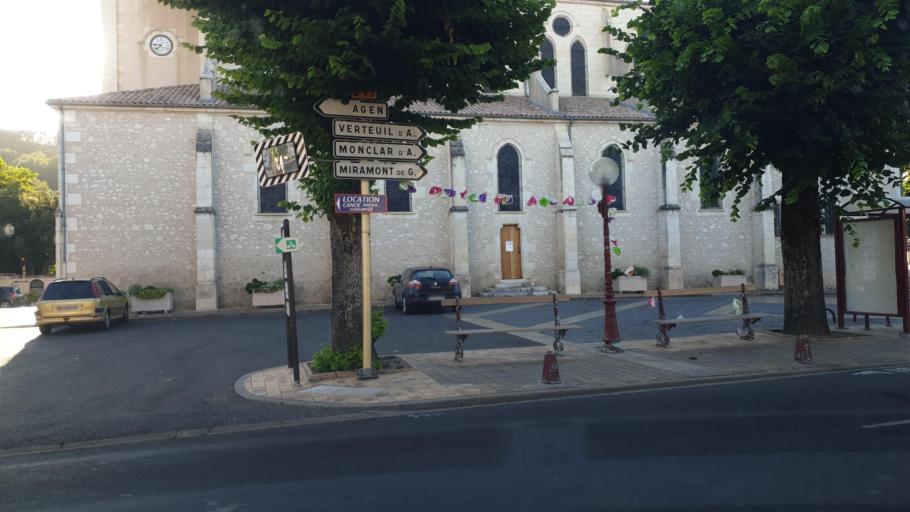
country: FR
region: Aquitaine
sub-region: Departement du Lot-et-Garonne
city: Castelmoron-sur-Lot
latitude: 44.3971
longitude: 0.4950
